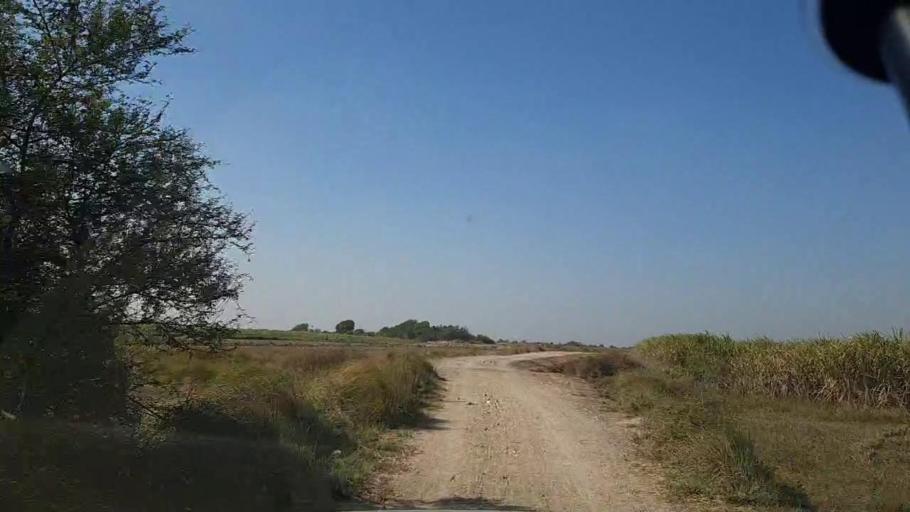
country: PK
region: Sindh
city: Chuhar Jamali
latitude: 24.5752
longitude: 68.0408
